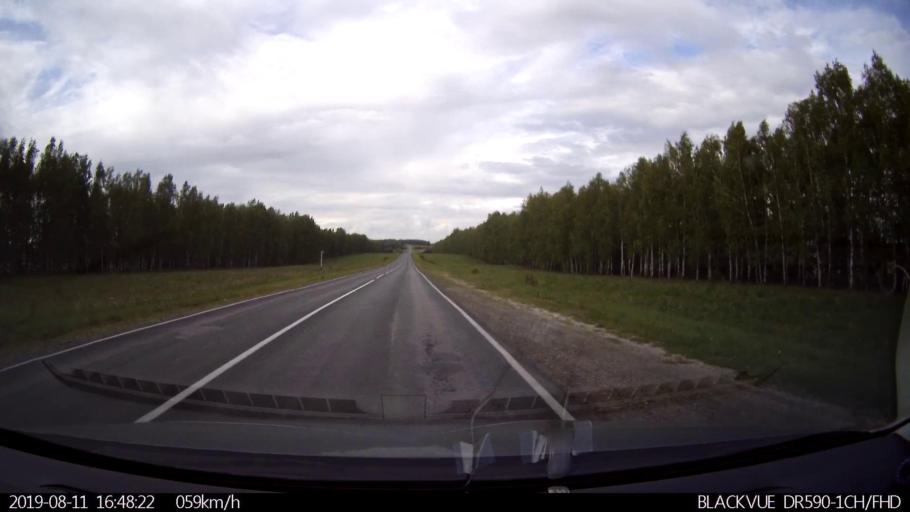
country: RU
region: Ulyanovsk
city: Mayna
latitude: 54.2084
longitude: 47.6921
